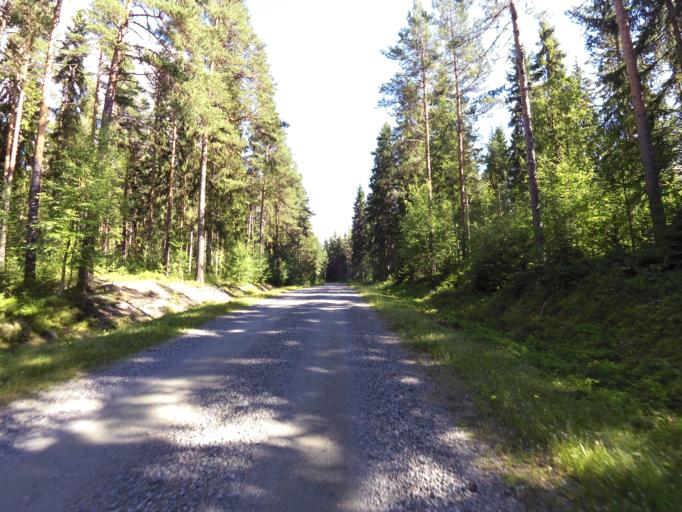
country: SE
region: Dalarna
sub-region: Faluns Kommun
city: Svardsjo
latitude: 60.6610
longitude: 15.8615
